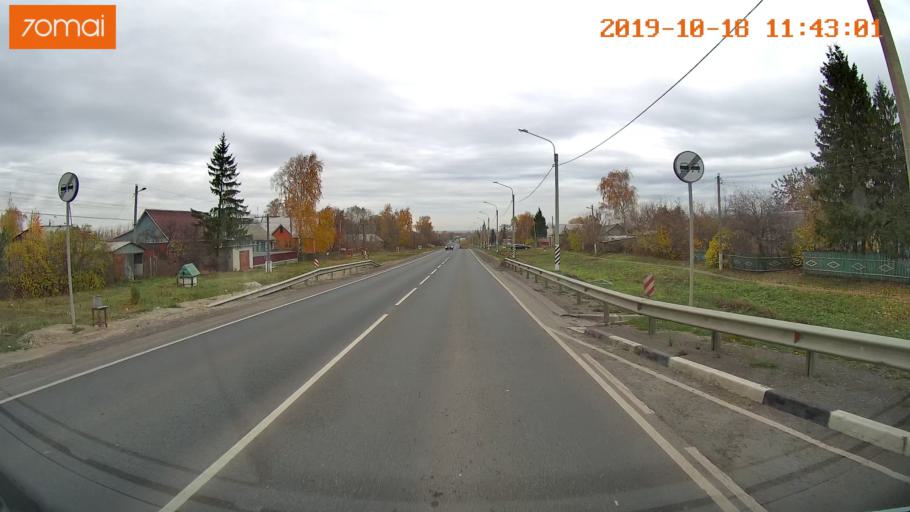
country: RU
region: Rjazan
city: Oktyabr'skiy
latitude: 54.1935
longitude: 38.9377
